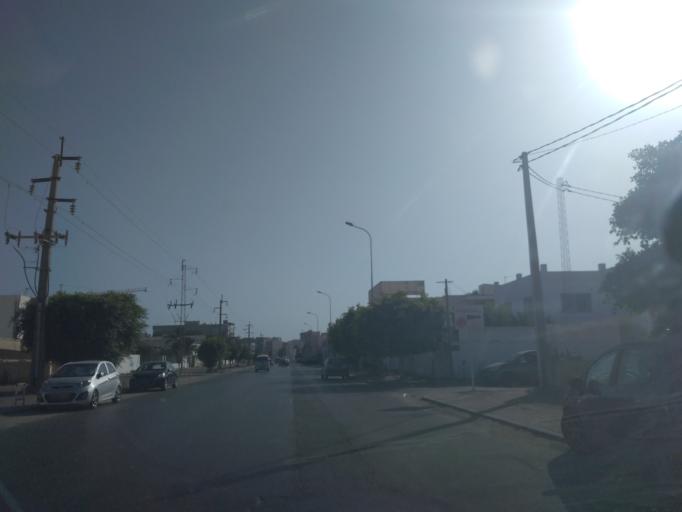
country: TN
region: Safaqis
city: Sfax
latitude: 34.7492
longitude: 10.7701
